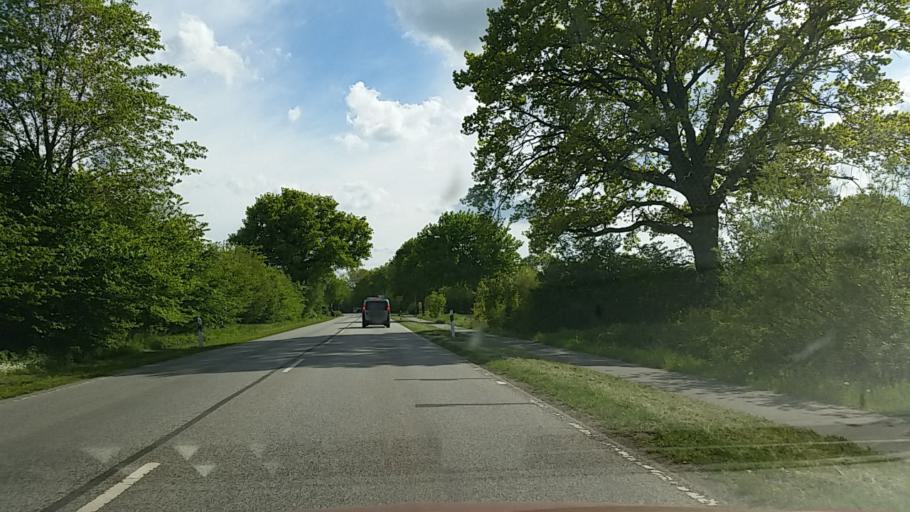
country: DE
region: Schleswig-Holstein
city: Bargteheide
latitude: 53.7405
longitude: 10.2624
